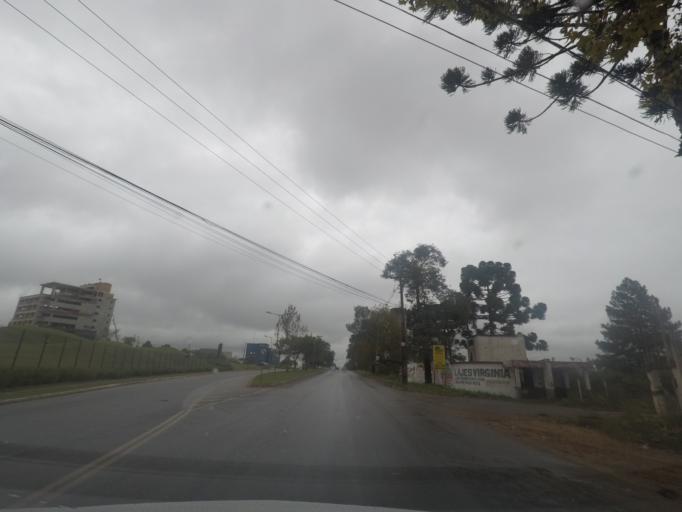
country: BR
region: Parana
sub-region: Pinhais
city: Pinhais
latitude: -25.3914
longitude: -49.1597
